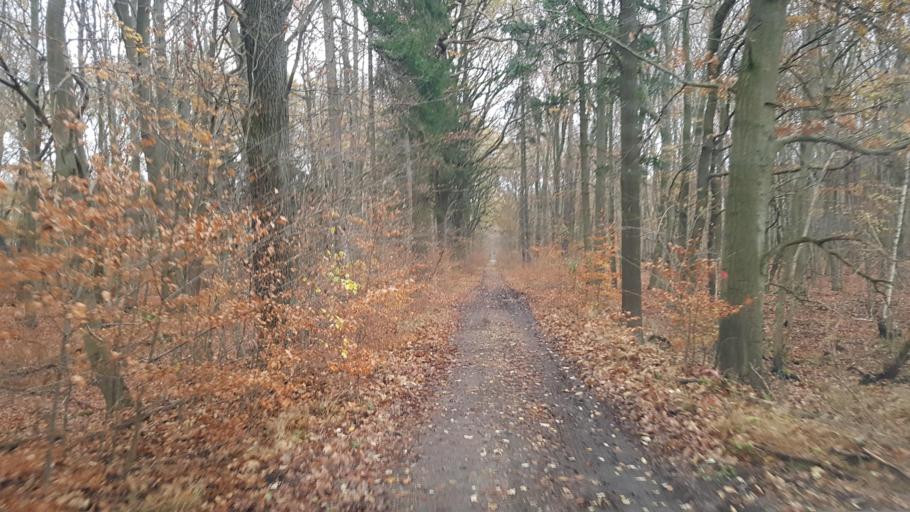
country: DE
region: Brandenburg
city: Crinitz
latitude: 51.7532
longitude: 13.7847
